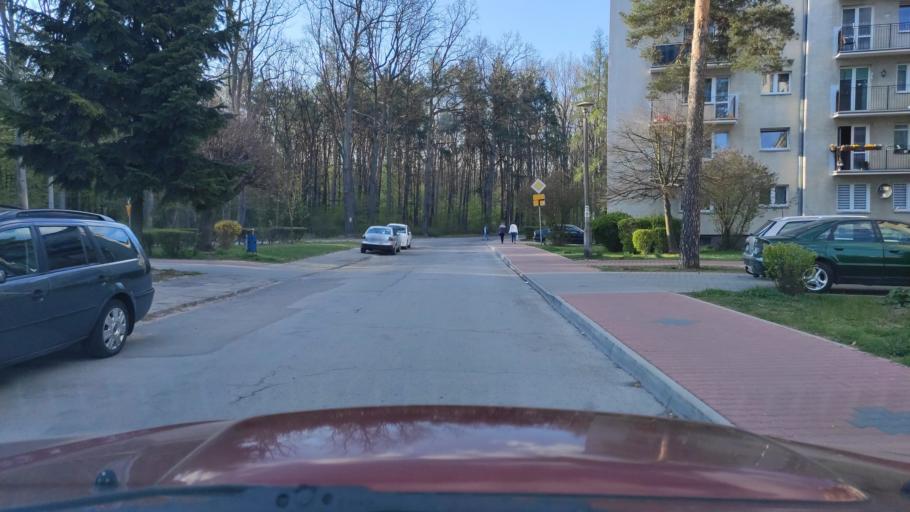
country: PL
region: Masovian Voivodeship
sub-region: Powiat radomski
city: Pionki
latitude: 51.4731
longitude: 21.4390
